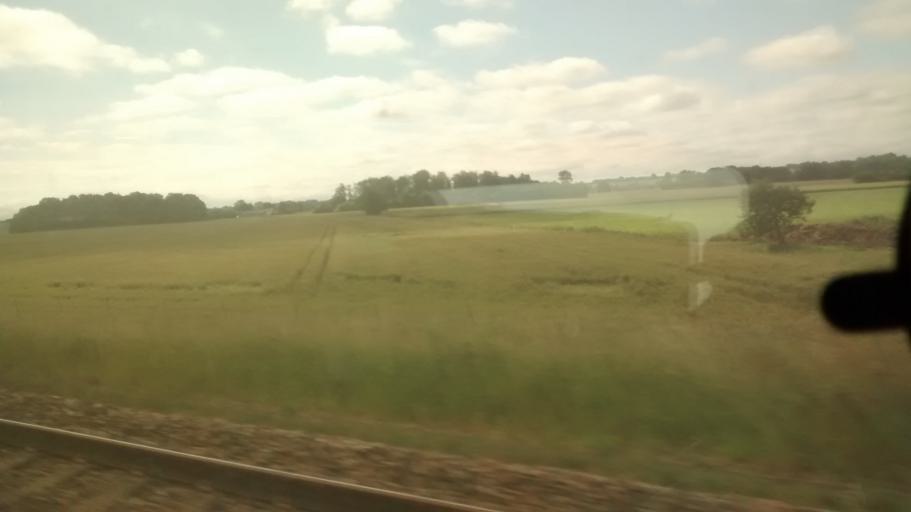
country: FR
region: Pays de la Loire
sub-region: Departement de la Sarthe
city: Vibraye
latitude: 48.0843
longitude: 0.7530
